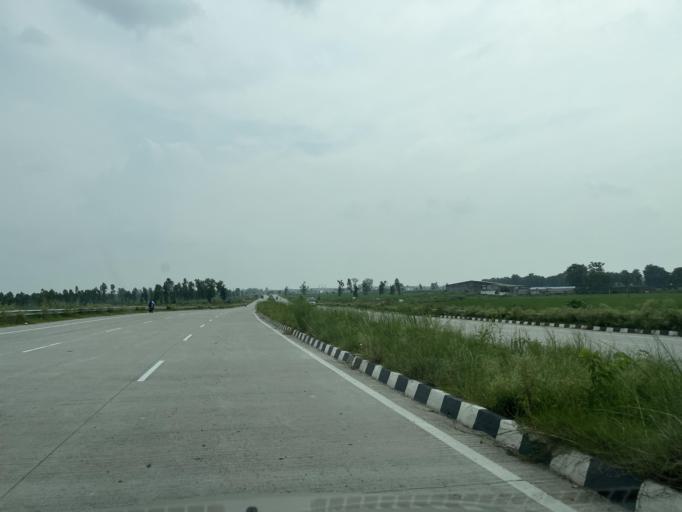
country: IN
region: Uttarakhand
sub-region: Udham Singh Nagar
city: Kashipur
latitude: 29.1874
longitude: 78.9396
